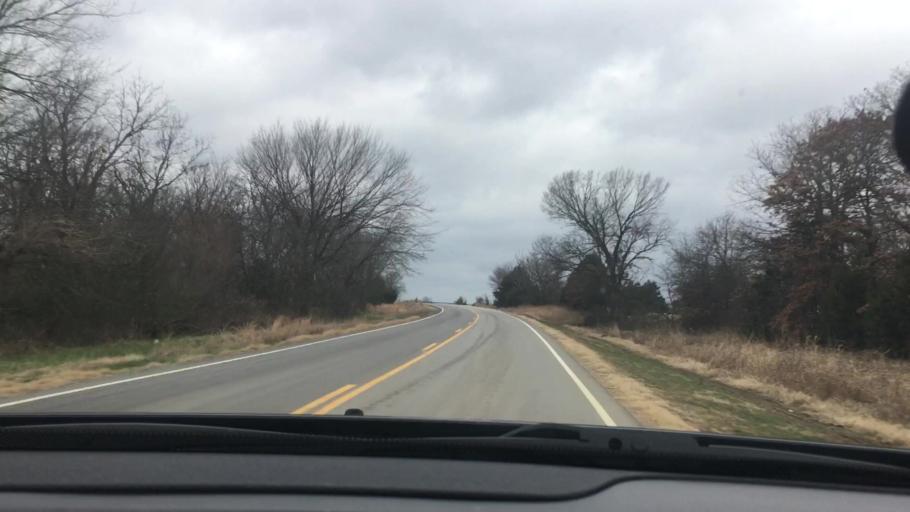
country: US
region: Oklahoma
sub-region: Atoka County
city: Atoka
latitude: 34.3792
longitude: -96.2857
